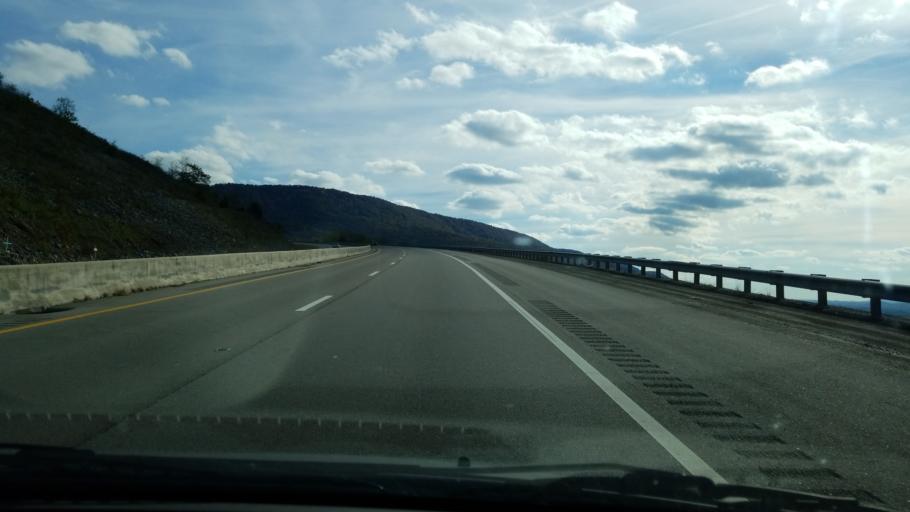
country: US
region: Tennessee
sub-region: Sequatchie County
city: Dunlap
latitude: 35.3736
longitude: -85.3323
